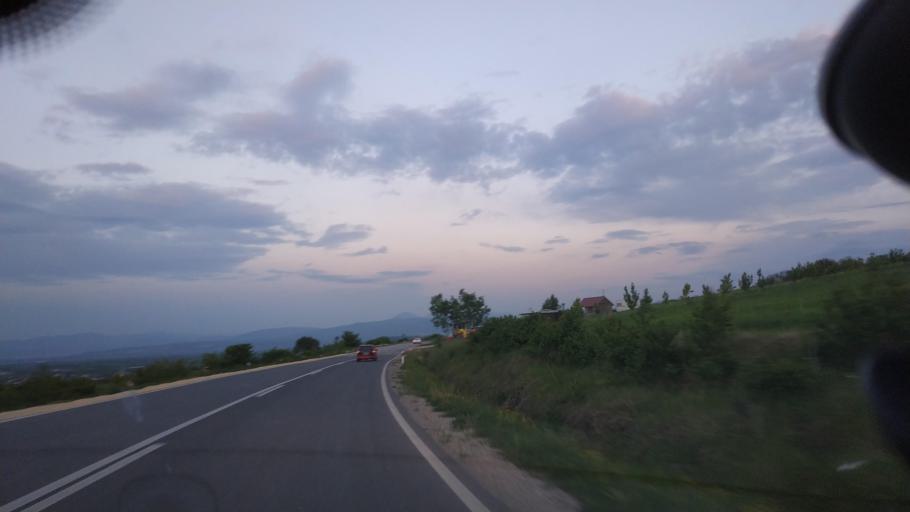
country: RS
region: Central Serbia
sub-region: Nisavski Okrug
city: Merosina
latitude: 43.2774
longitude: 21.6877
